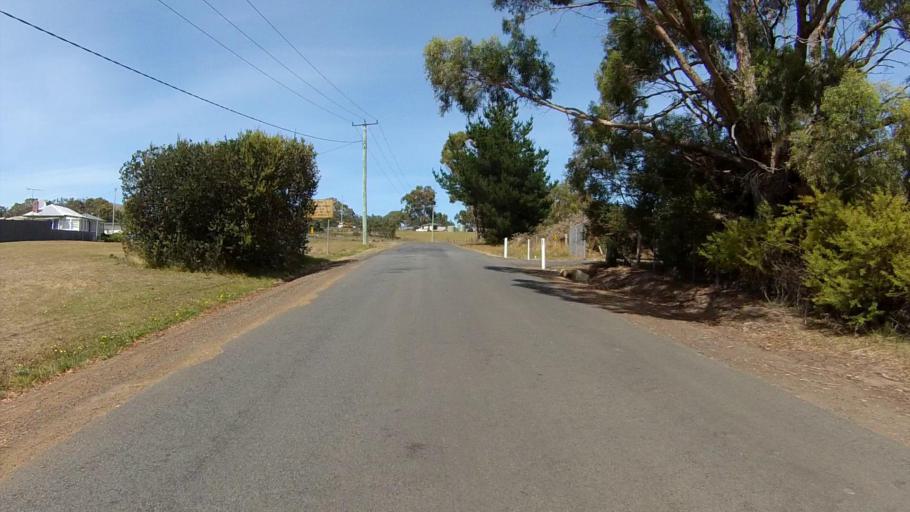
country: AU
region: Tasmania
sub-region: Sorell
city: Sorell
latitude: -42.6114
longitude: 147.7272
